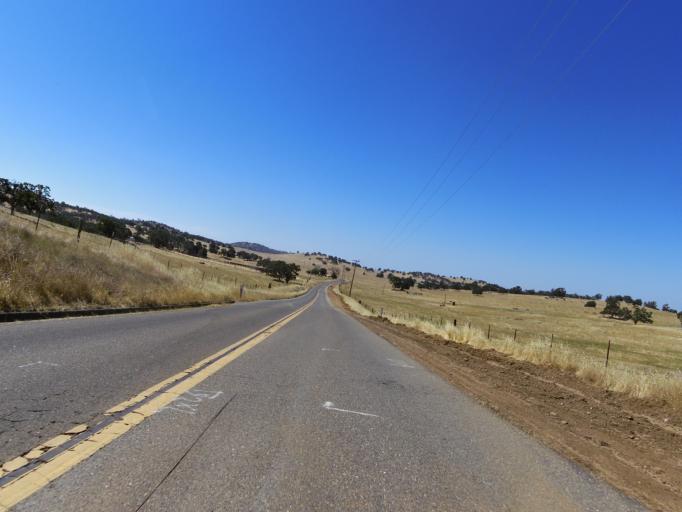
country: US
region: California
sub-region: Merced County
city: Planada
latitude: 37.6109
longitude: -120.3087
